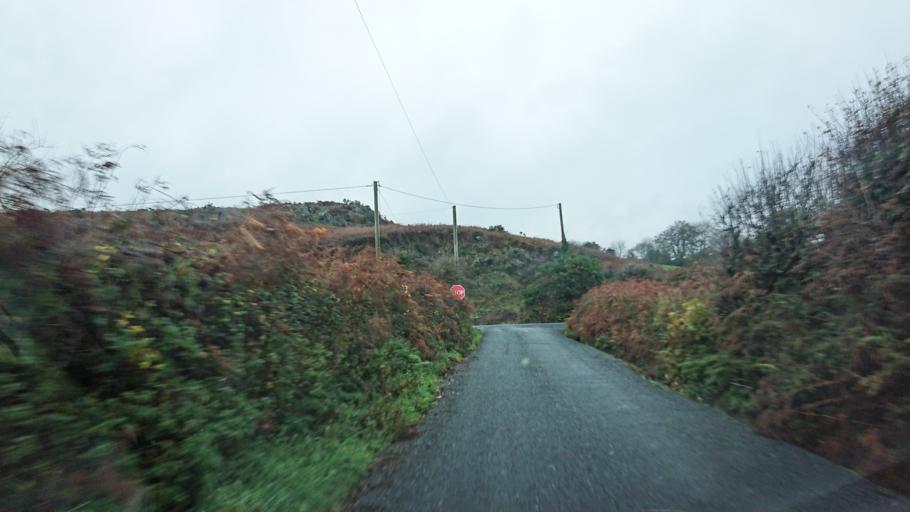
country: IE
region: Munster
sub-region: Waterford
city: Tra Mhor
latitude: 52.2028
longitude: -7.1781
